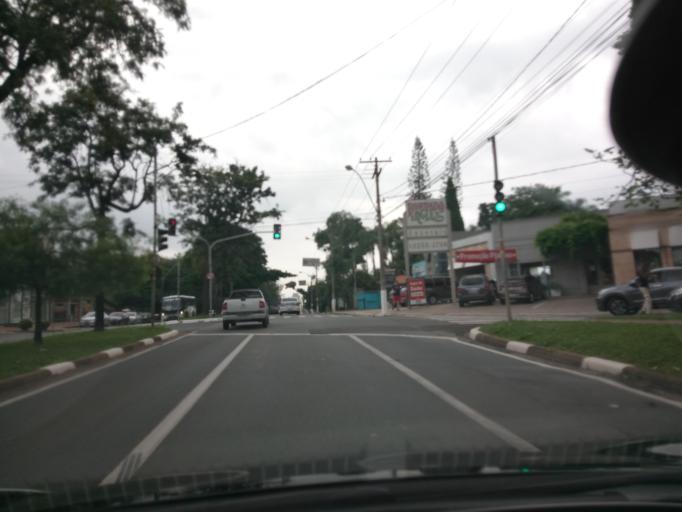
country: BR
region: Sao Paulo
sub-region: Campinas
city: Campinas
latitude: -22.9055
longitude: -47.0377
